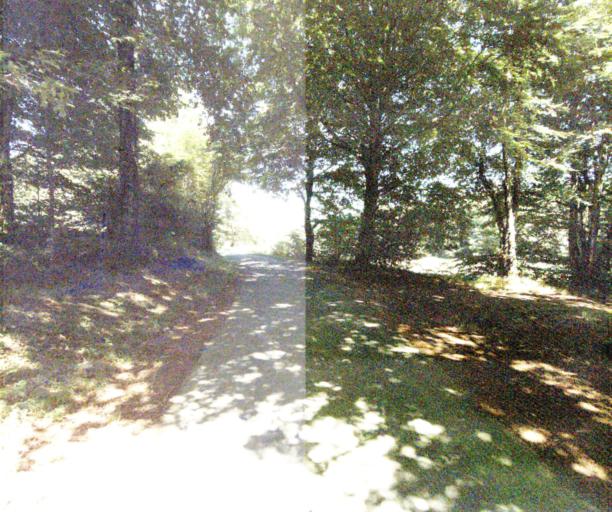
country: FR
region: Midi-Pyrenees
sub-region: Departement du Tarn
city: Dourgne
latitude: 43.4286
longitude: 2.1571
